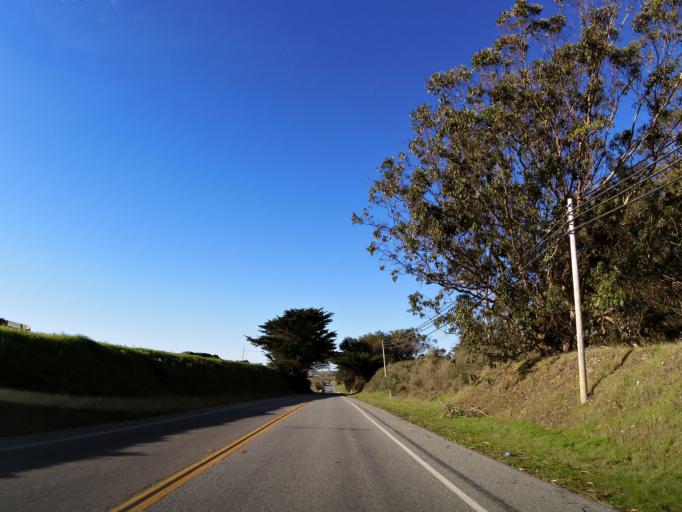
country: US
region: California
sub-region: Santa Cruz County
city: Bonny Doon
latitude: 37.0217
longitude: -122.2089
